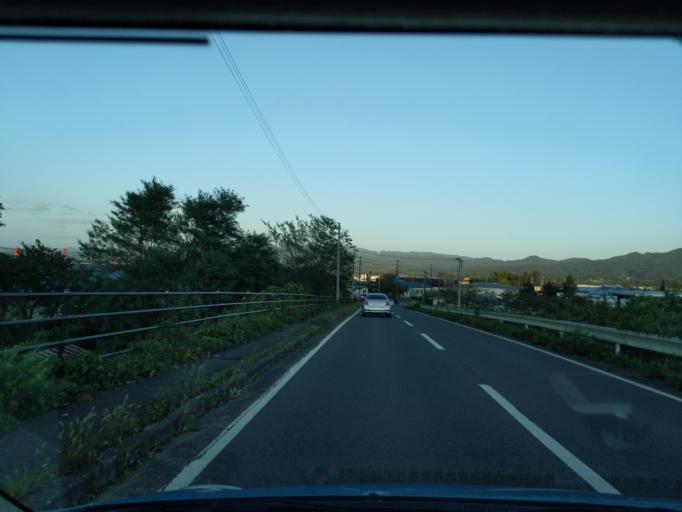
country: JP
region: Iwate
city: Mizusawa
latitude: 39.0464
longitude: 141.1265
